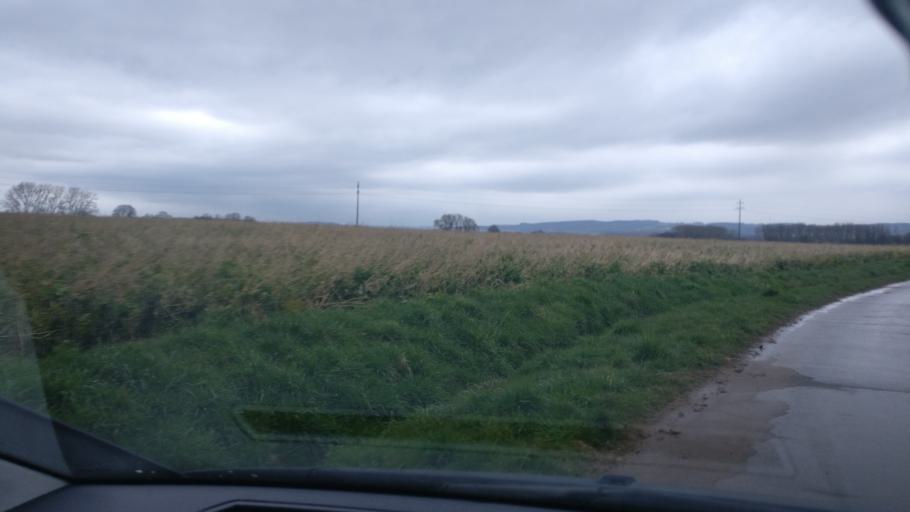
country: DE
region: North Rhine-Westphalia
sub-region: Regierungsbezirk Detmold
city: Lage
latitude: 52.0198
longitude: 8.7923
